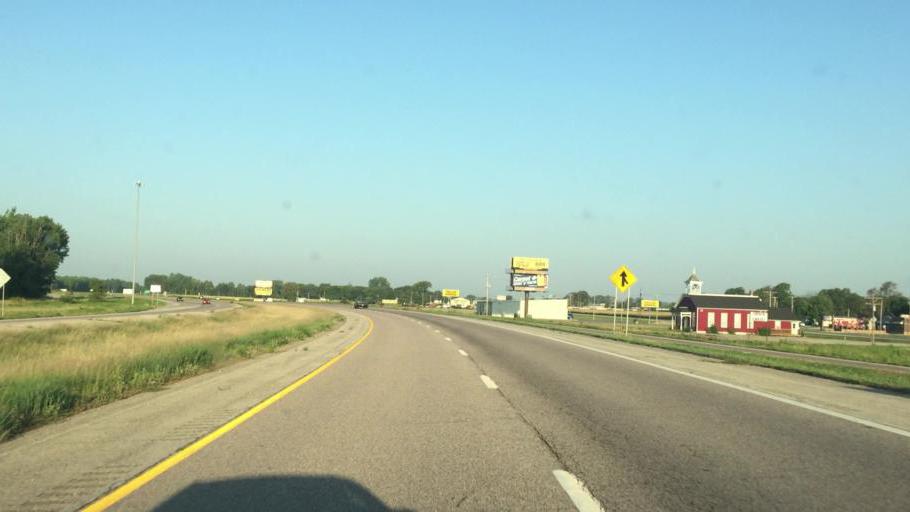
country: US
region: Kansas
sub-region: Doniphan County
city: Elwood
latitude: 39.7498
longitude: -94.8697
